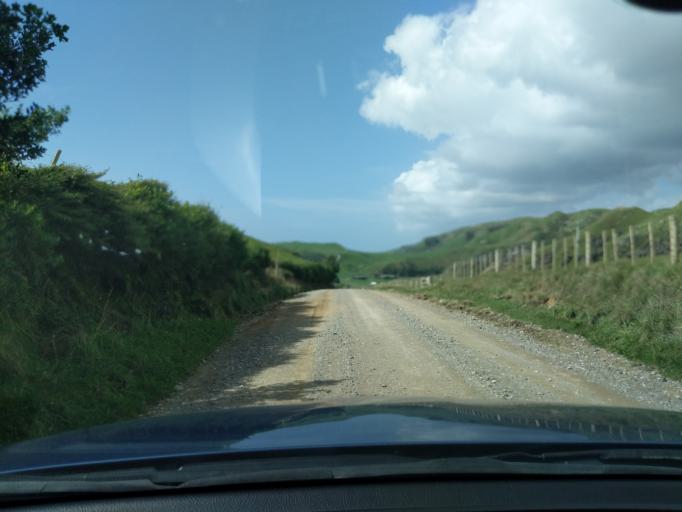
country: NZ
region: Tasman
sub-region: Tasman District
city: Takaka
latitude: -40.6482
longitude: 172.4275
